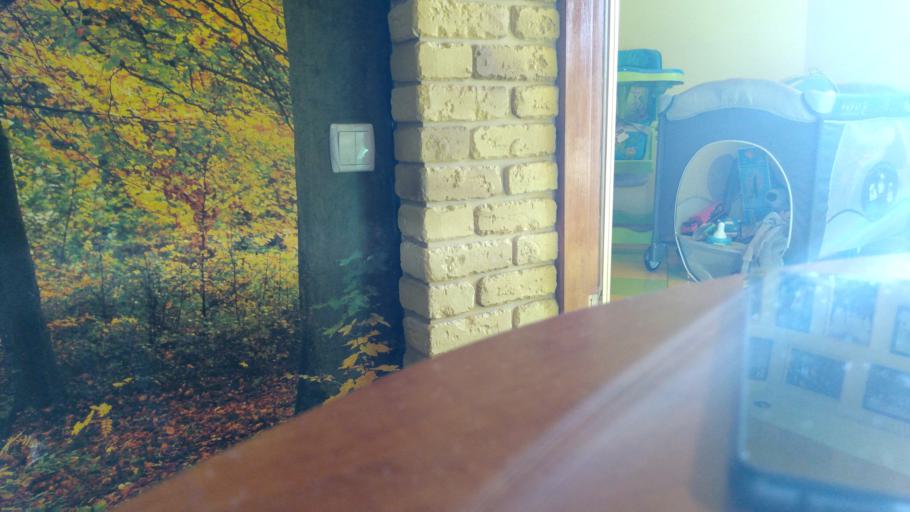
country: RU
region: Tverskaya
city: Likhoslavl'
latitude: 57.1193
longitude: 35.6641
